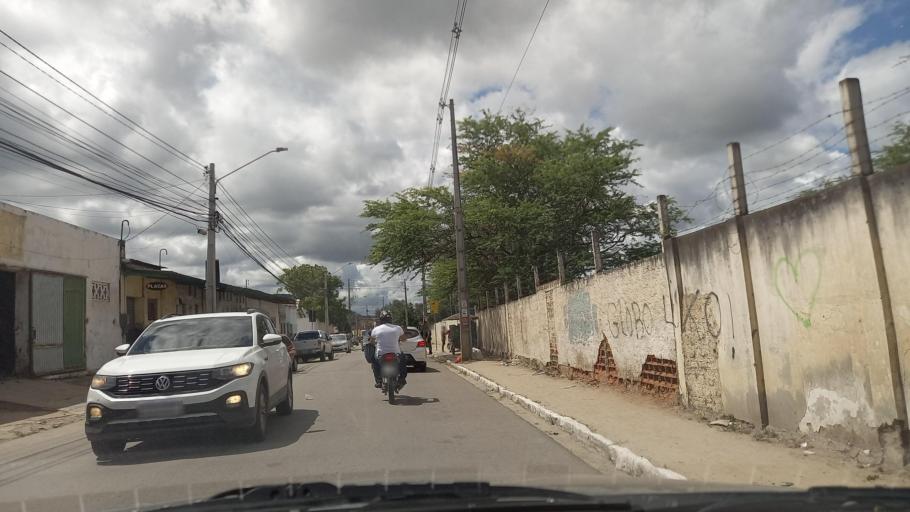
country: BR
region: Pernambuco
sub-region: Caruaru
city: Caruaru
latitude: -8.2805
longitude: -35.9476
